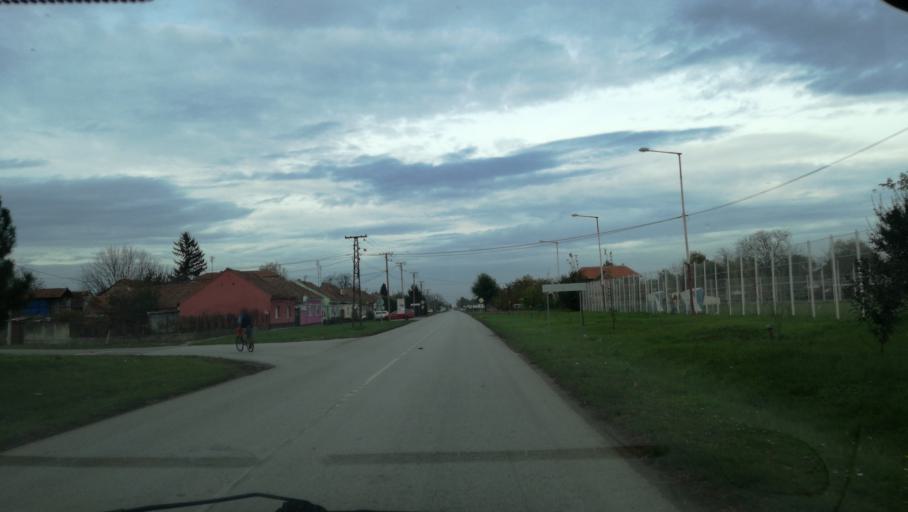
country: RS
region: Autonomna Pokrajina Vojvodina
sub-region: Severnobanatski Okrug
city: Kikinda
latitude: 45.8391
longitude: 20.4551
